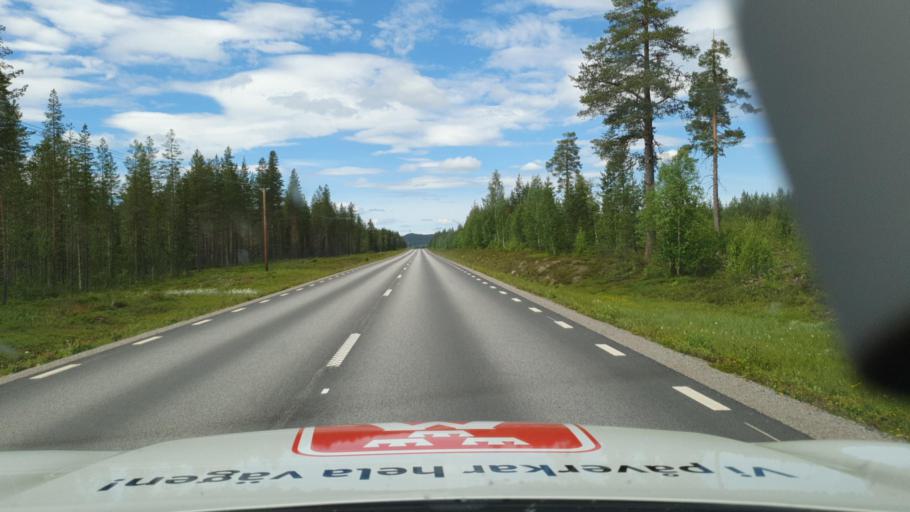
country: SE
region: Vaesterbotten
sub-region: Norsjo Kommun
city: Norsjoe
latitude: 65.2405
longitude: 19.7142
